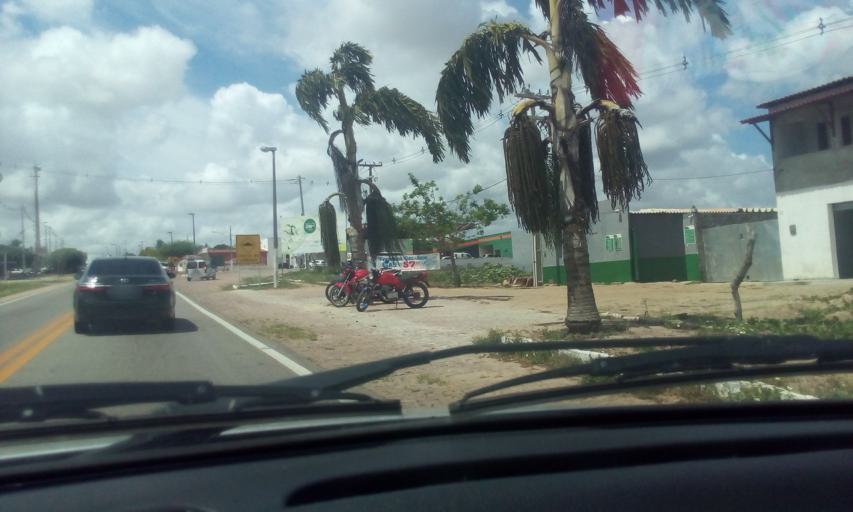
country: BR
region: Rio Grande do Norte
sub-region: Sao Paulo Do Potengi
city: Sao Paulo do Potengi
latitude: -5.9811
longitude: -35.5796
